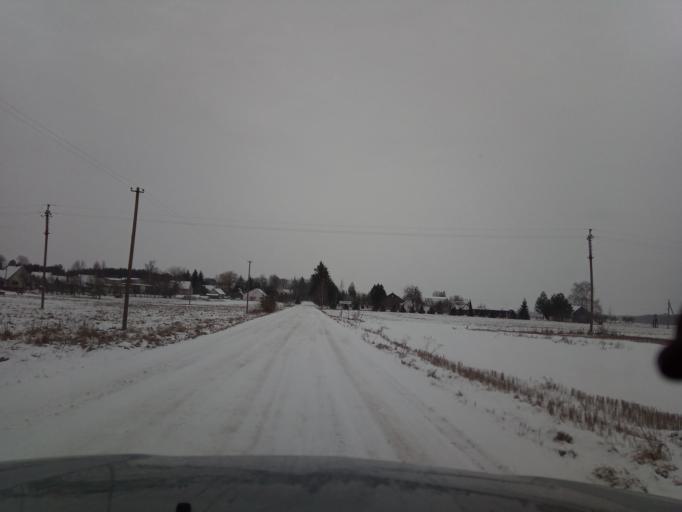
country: LT
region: Panevezys
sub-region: Panevezys City
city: Panevezys
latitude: 55.6171
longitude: 24.3669
